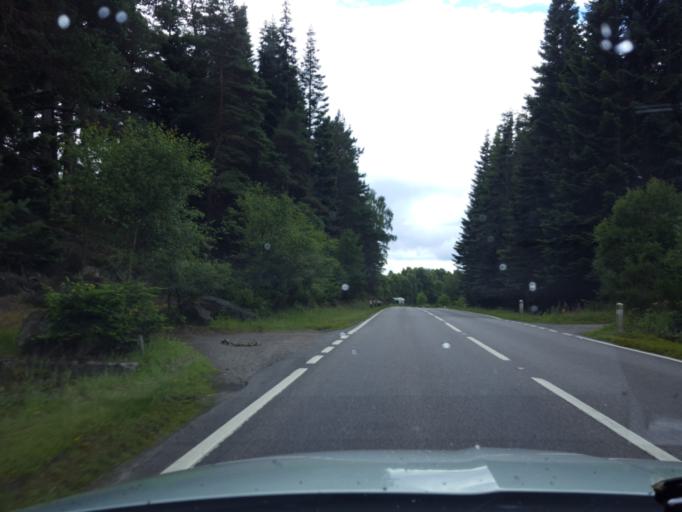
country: GB
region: Scotland
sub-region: Highland
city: Aviemore
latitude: 57.2365
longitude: -3.8070
